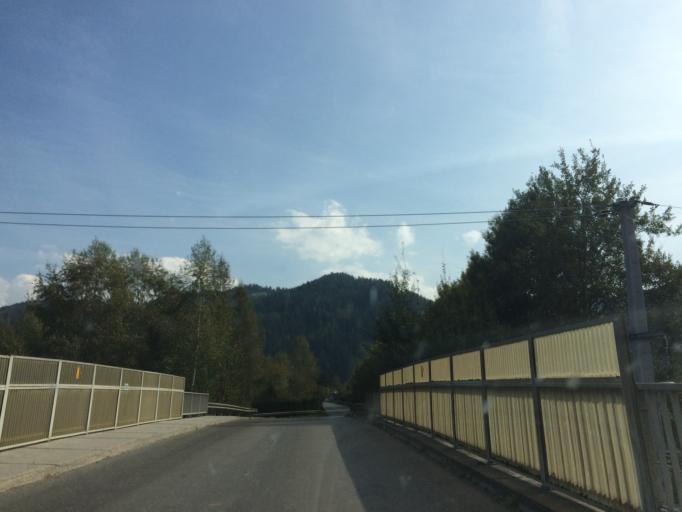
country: AT
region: Styria
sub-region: Politischer Bezirk Leoben
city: Kraubath an der Mur
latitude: 47.3039
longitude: 14.9434
